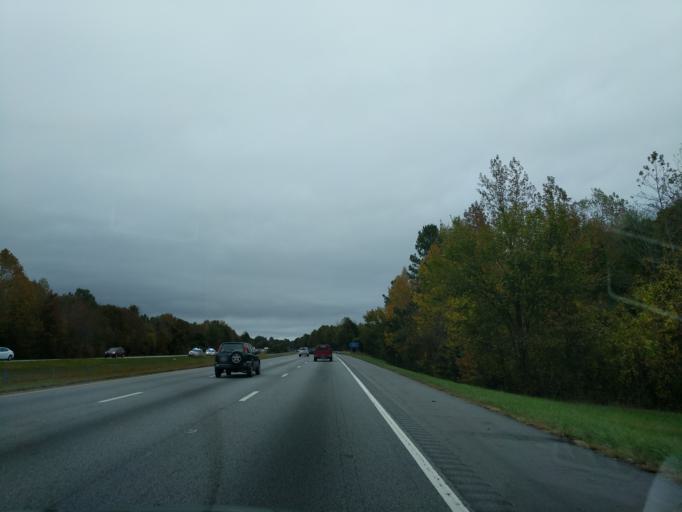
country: US
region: North Carolina
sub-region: Randolph County
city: Archdale
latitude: 35.8965
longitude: -79.9702
